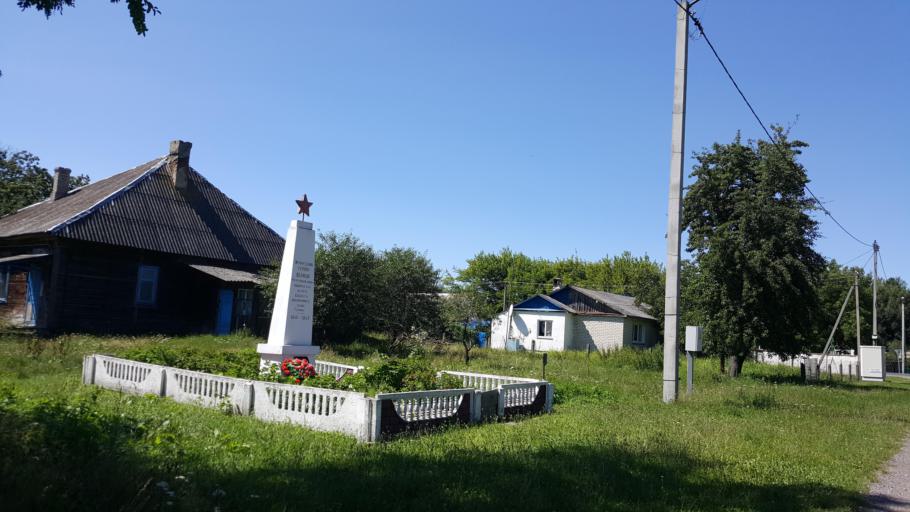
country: BY
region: Brest
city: Charnawchytsy
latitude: 52.2061
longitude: 23.8279
